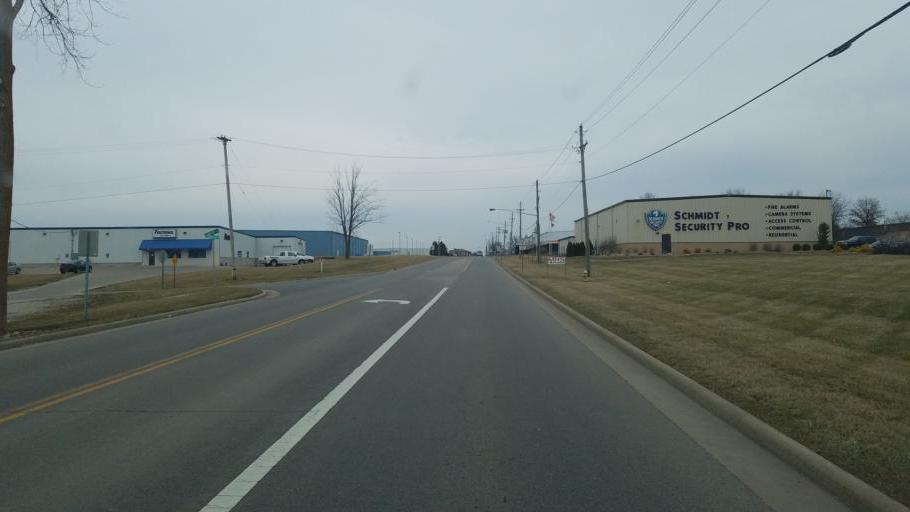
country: US
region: Ohio
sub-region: Richland County
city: Lincoln Heights
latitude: 40.8012
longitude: -82.5134
